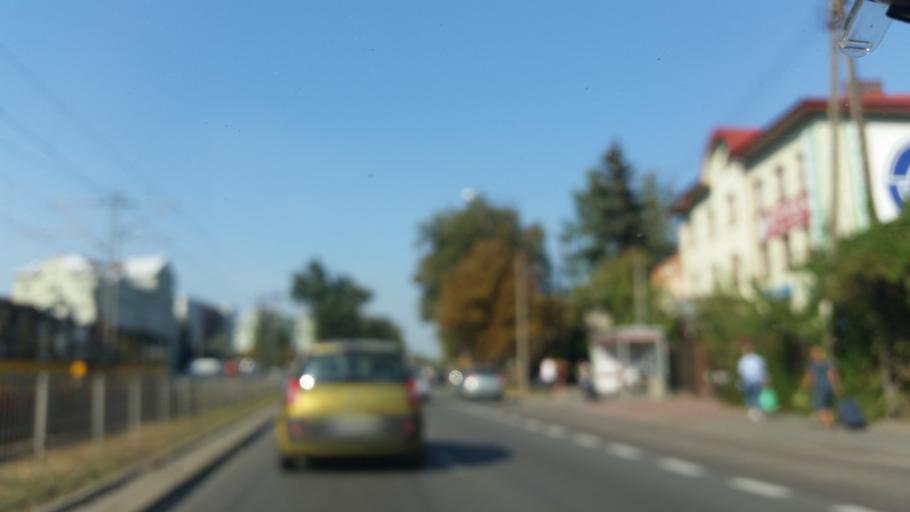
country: PL
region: Masovian Voivodeship
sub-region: Warszawa
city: Bemowo
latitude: 52.2296
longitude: 20.9153
